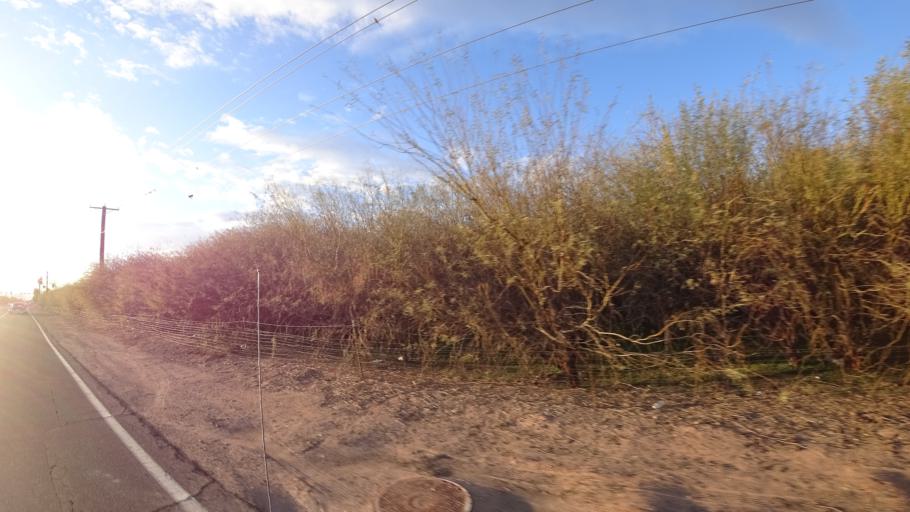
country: US
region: Arizona
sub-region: Maricopa County
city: Glendale
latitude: 33.5452
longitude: -112.2176
